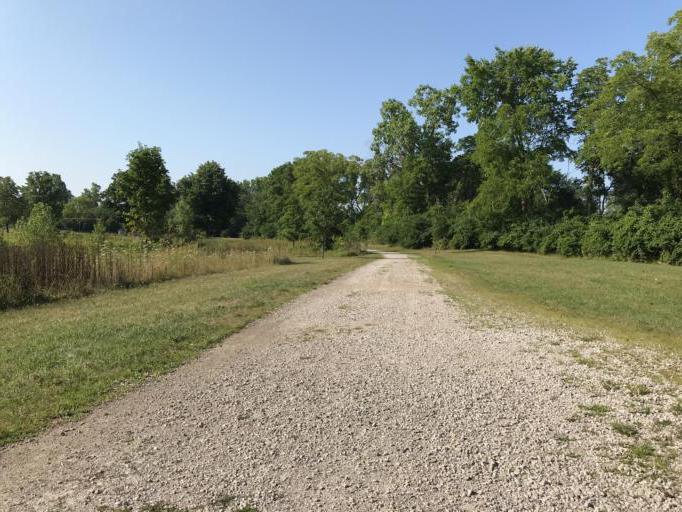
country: US
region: Michigan
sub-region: Washtenaw County
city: Ann Arbor
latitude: 42.2413
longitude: -83.7126
